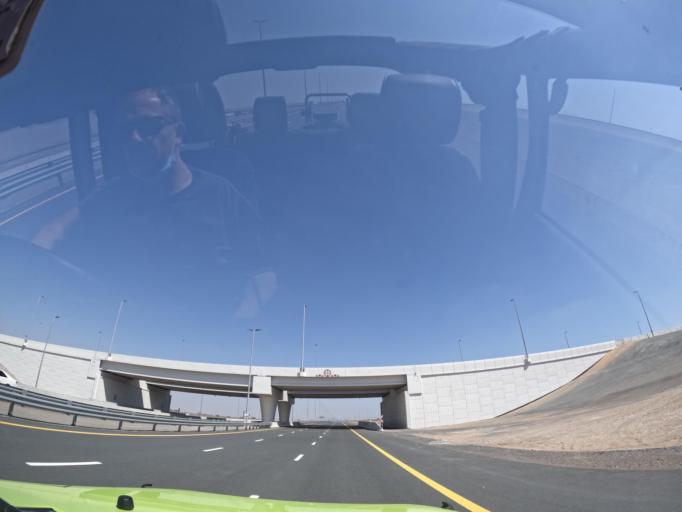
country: AE
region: Ash Shariqah
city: Adh Dhayd
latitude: 25.0717
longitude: 55.9093
